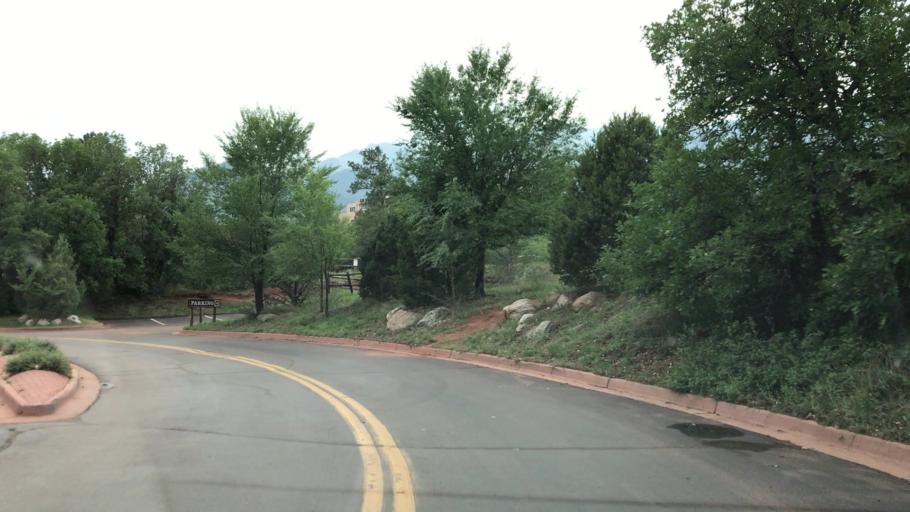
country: US
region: Colorado
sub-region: El Paso County
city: Manitou Springs
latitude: 38.8638
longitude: -104.8933
